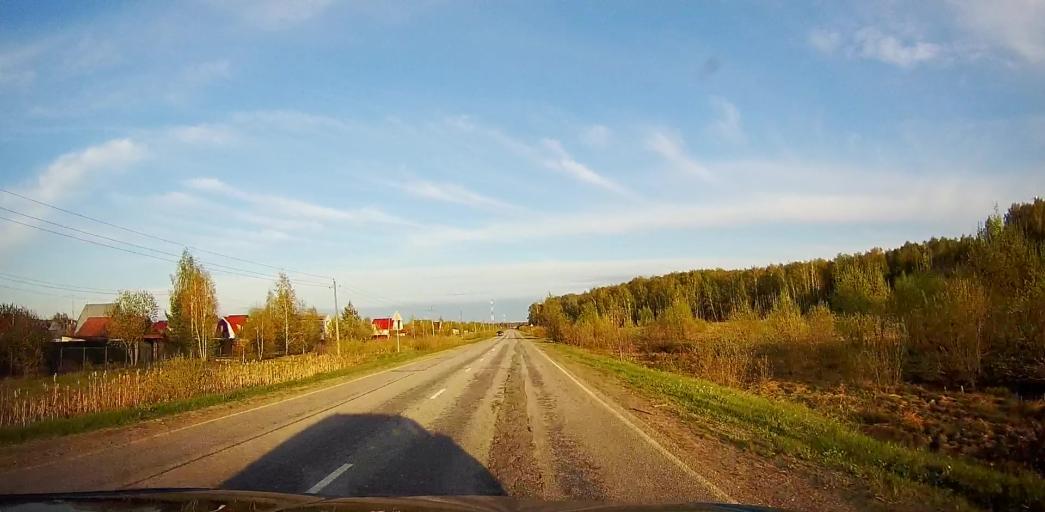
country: RU
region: Moskovskaya
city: Meshcherino
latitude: 55.2393
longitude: 38.3417
